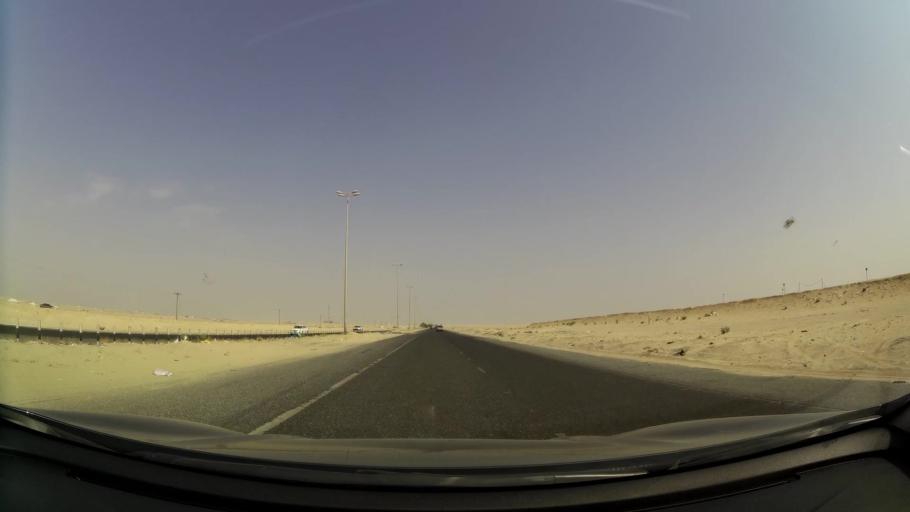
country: KW
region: Al Ahmadi
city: Al Wafrah
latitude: 28.8294
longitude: 48.0529
